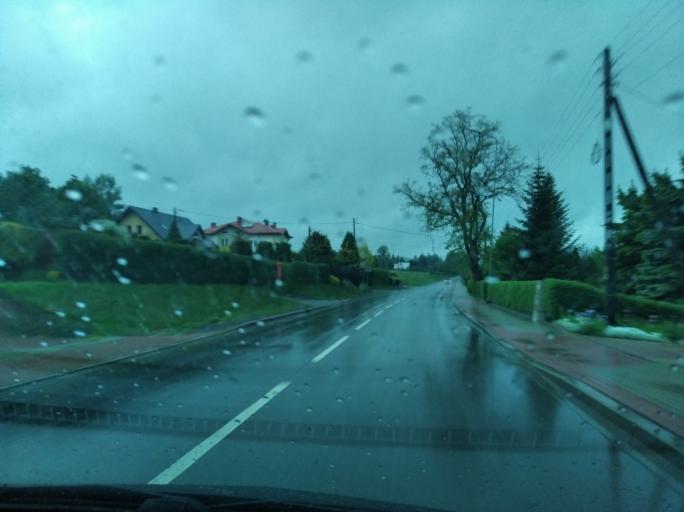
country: PL
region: Subcarpathian Voivodeship
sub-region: Krosno
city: Krosno
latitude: 49.7006
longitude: 21.7860
